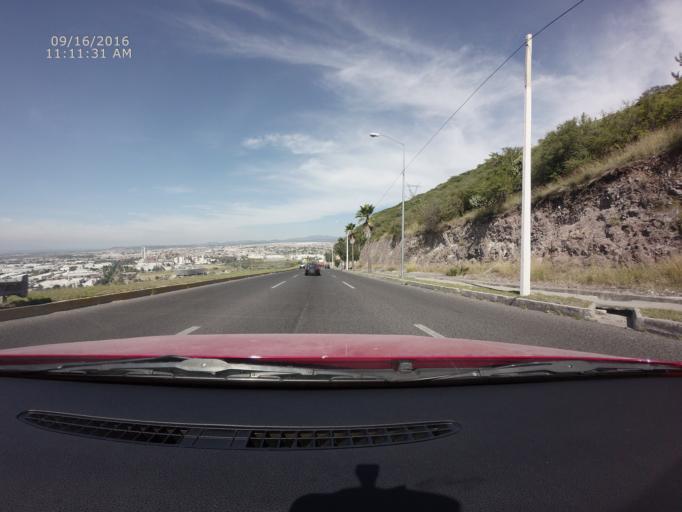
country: MX
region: Queretaro
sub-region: Queretaro
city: Sergio Villasenor
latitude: 20.6421
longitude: -100.4222
